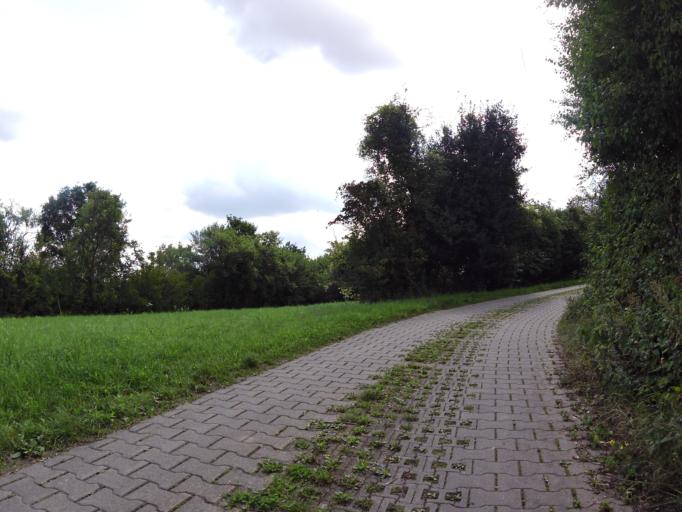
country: DE
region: Bavaria
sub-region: Regierungsbezirk Unterfranken
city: Margetshochheim
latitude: 49.8328
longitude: 9.8581
